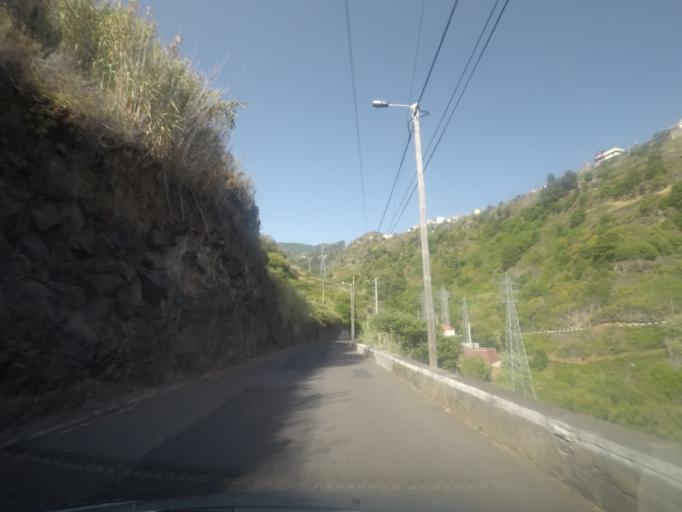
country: PT
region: Madeira
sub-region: Calheta
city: Arco da Calheta
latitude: 32.7300
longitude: -17.1655
